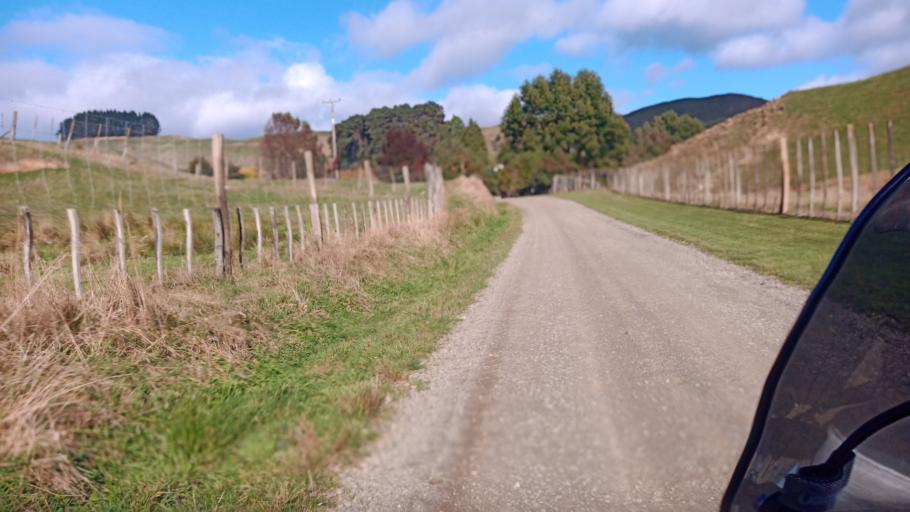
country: NZ
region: Bay of Plenty
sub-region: Opotiki District
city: Opotiki
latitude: -38.4609
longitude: 177.3851
